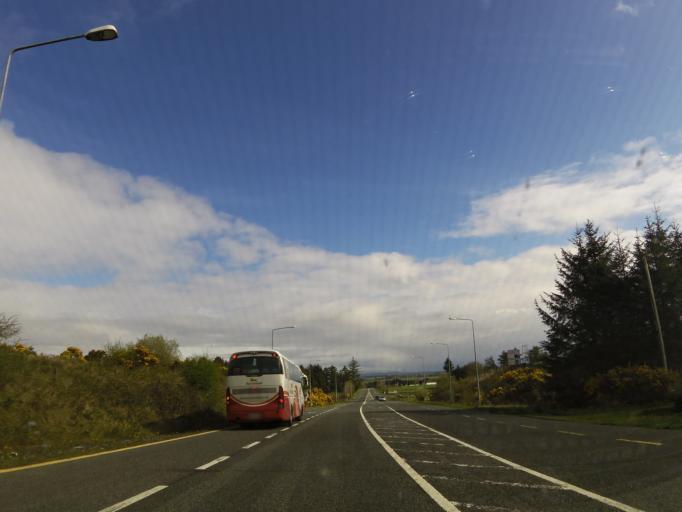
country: IE
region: Connaught
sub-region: Sligo
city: Tobercurry
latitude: 53.9139
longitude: -8.7921
